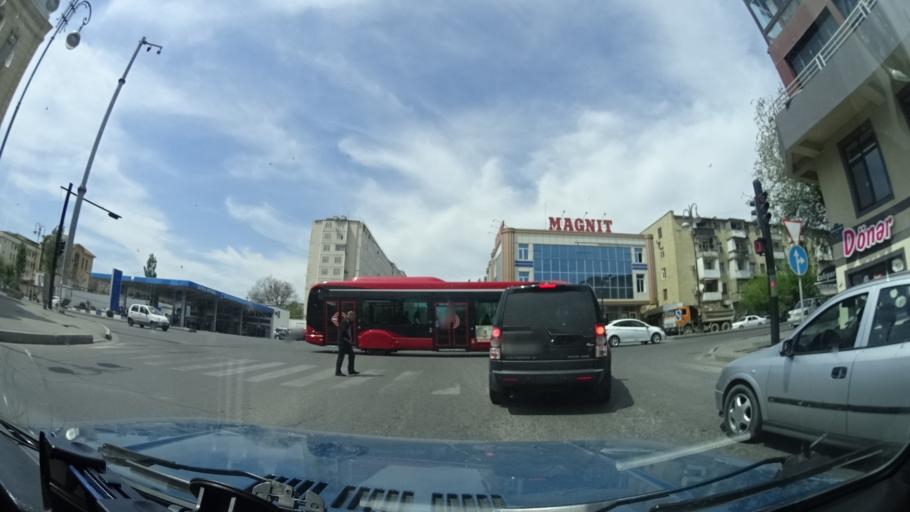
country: AZ
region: Baki
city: Khodzhi-Gasan
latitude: 40.3946
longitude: 49.8024
